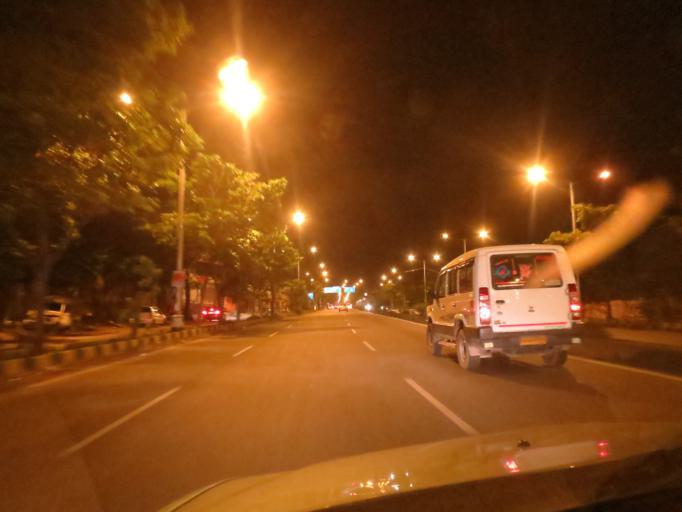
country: IN
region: Karnataka
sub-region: Bangalore Urban
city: Bangalore
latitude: 13.0082
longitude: 77.6626
